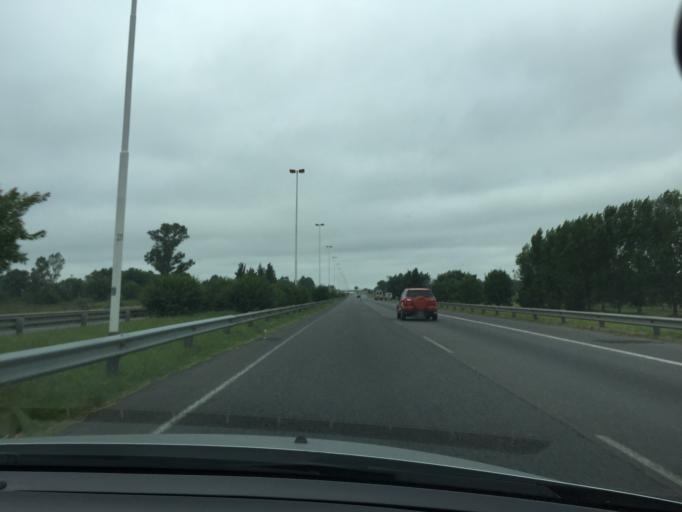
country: AR
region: Buenos Aires
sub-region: Partido de Ezeiza
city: Ezeiza
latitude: -34.8692
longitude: -58.5785
